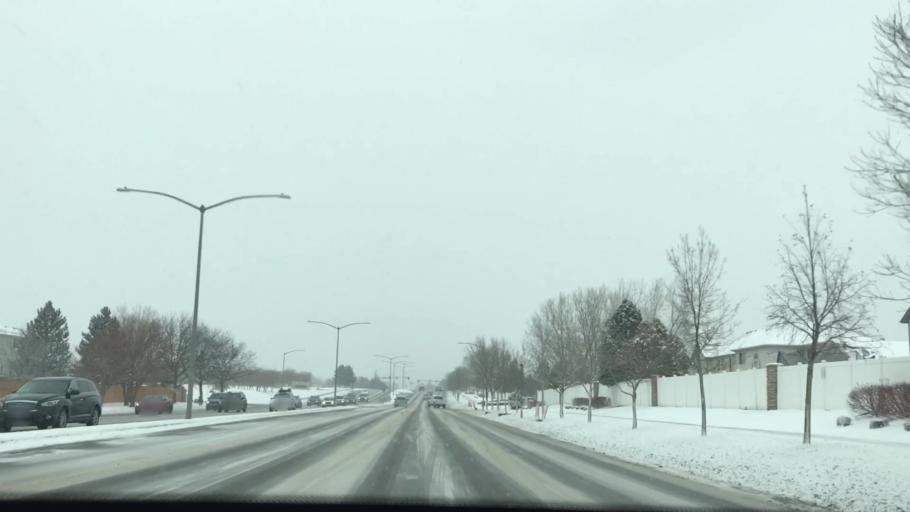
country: US
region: Colorado
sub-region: Broomfield County
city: Broomfield
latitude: 39.9078
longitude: -105.0529
